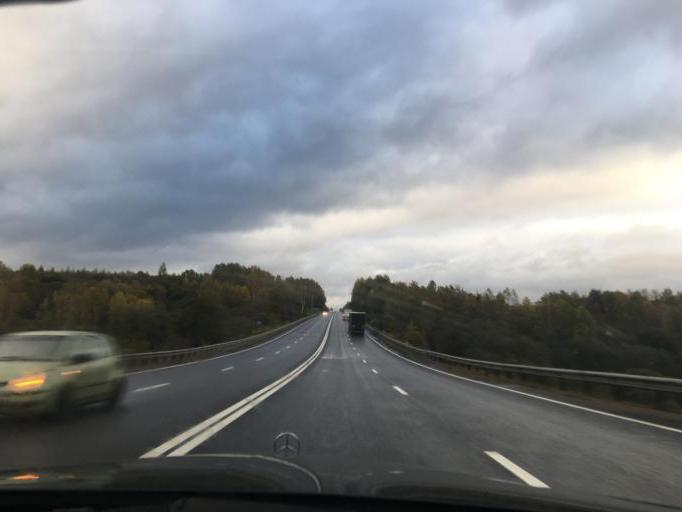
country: RU
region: Smolensk
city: Pechersk
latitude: 54.8853
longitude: 32.0829
